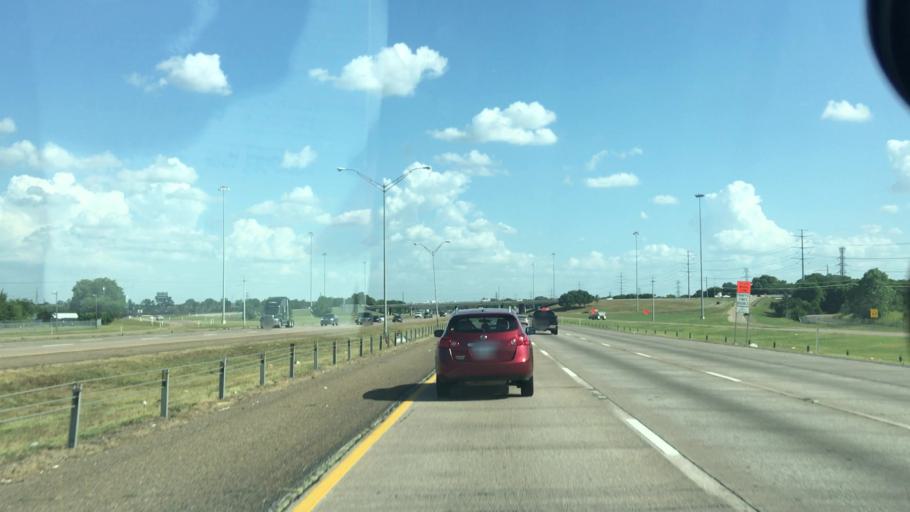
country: US
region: Texas
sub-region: Dallas County
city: Hutchins
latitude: 32.7062
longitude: -96.7547
